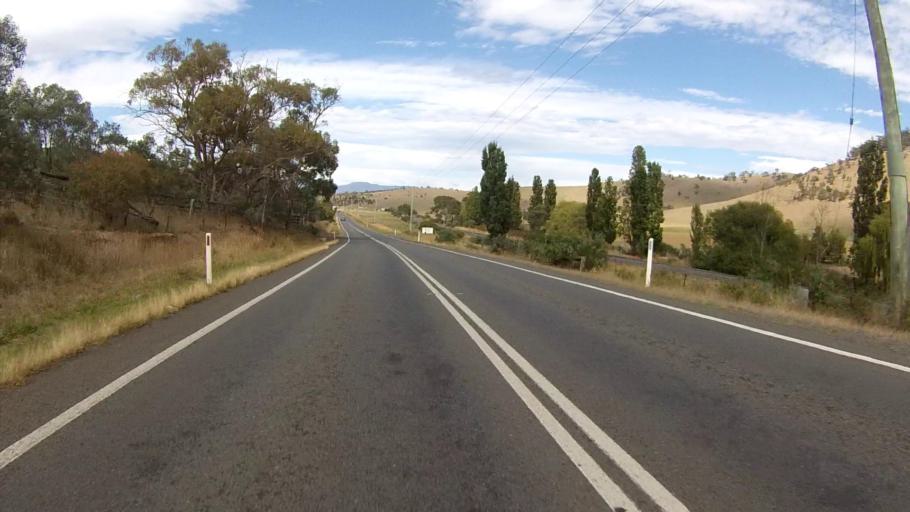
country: AU
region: Tasmania
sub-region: Brighton
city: Old Beach
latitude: -42.6718
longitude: 147.3624
